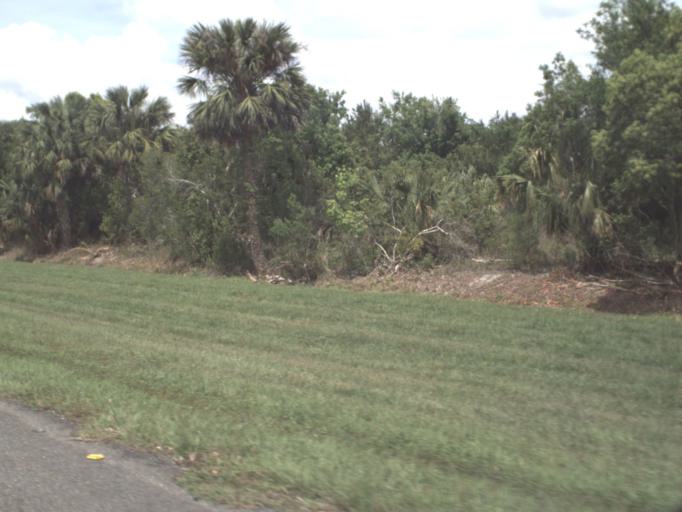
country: US
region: Florida
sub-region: Flagler County
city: Bunnell
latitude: 29.3374
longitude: -81.3108
